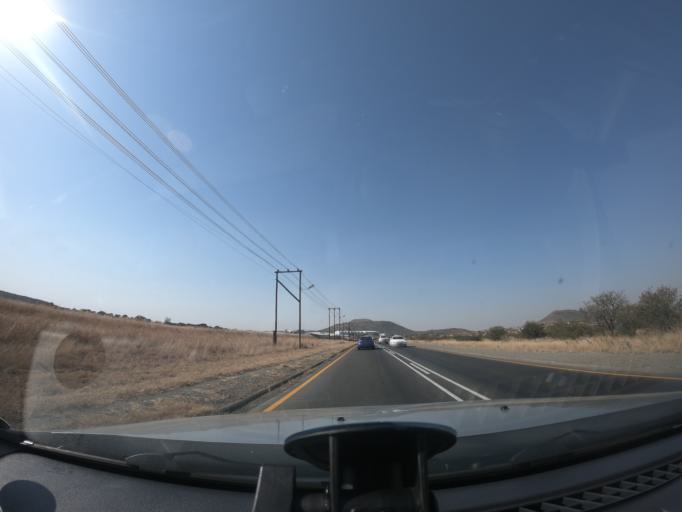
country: ZA
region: KwaZulu-Natal
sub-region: uThukela District Municipality
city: Ladysmith
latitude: -28.5467
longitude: 29.8210
